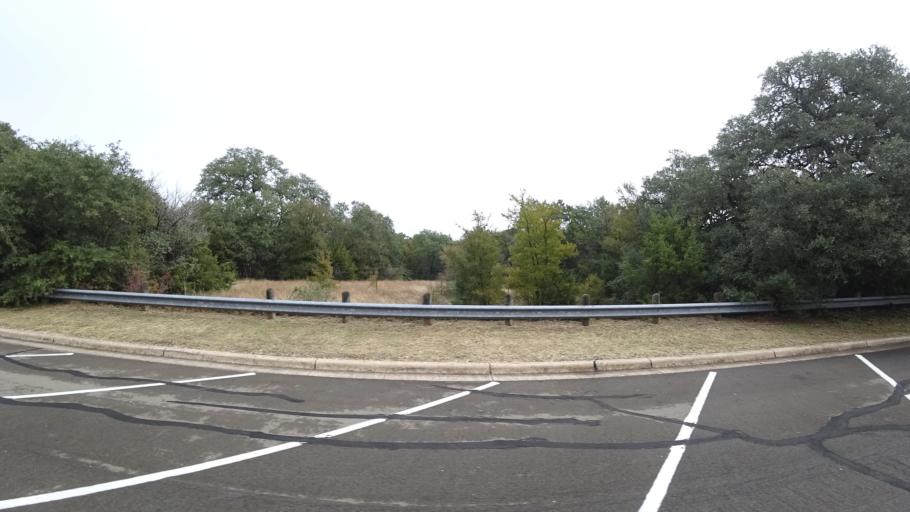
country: US
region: Texas
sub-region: Travis County
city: Shady Hollow
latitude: 30.1874
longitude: -97.8715
